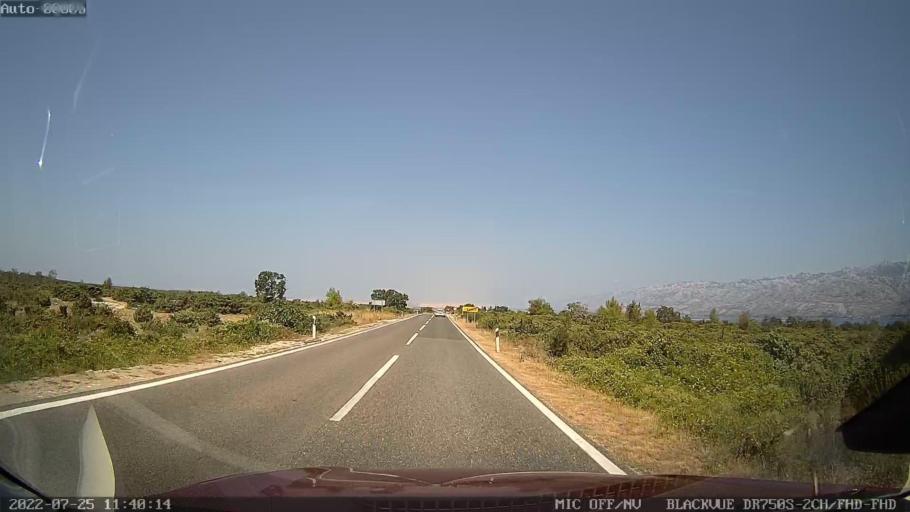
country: HR
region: Zadarska
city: Razanac
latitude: 44.2618
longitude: 15.3629
